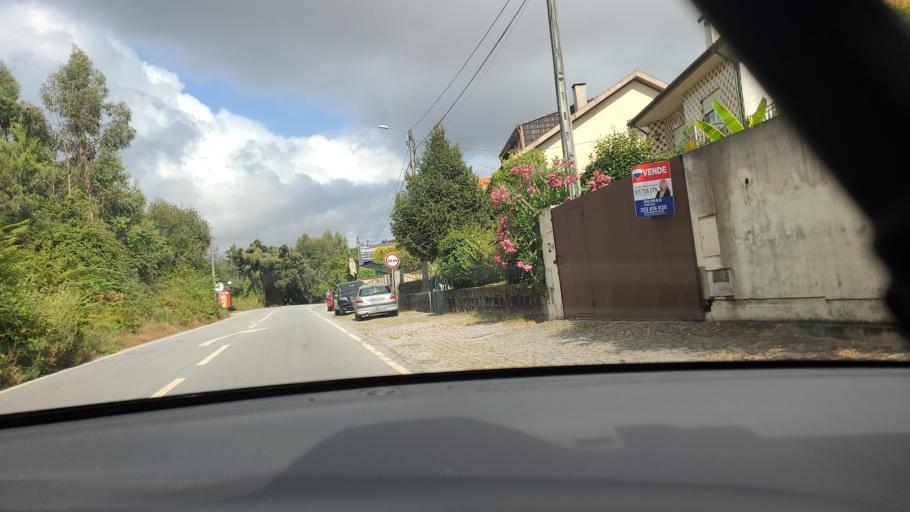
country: PT
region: Braga
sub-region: Braga
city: Adaufe
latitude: 41.5767
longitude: -8.4140
